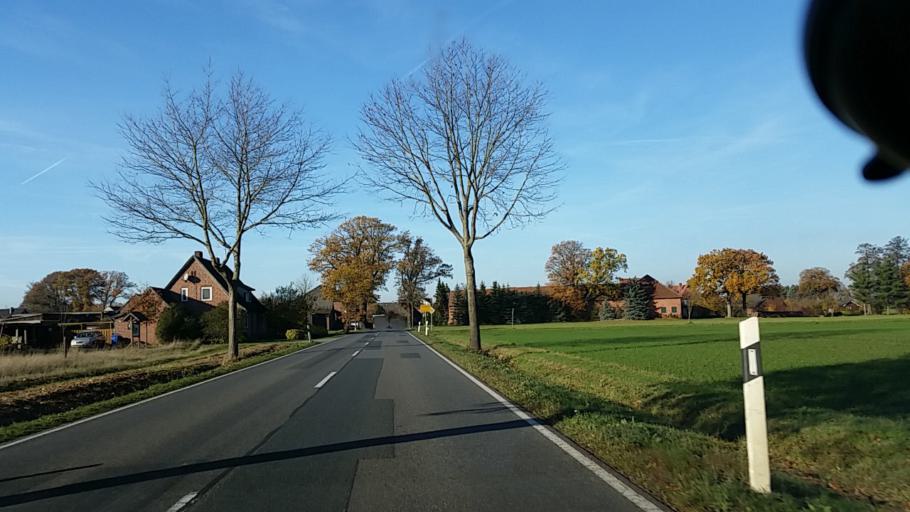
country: DE
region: Lower Saxony
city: Wittingen
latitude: 52.7076
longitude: 10.7731
